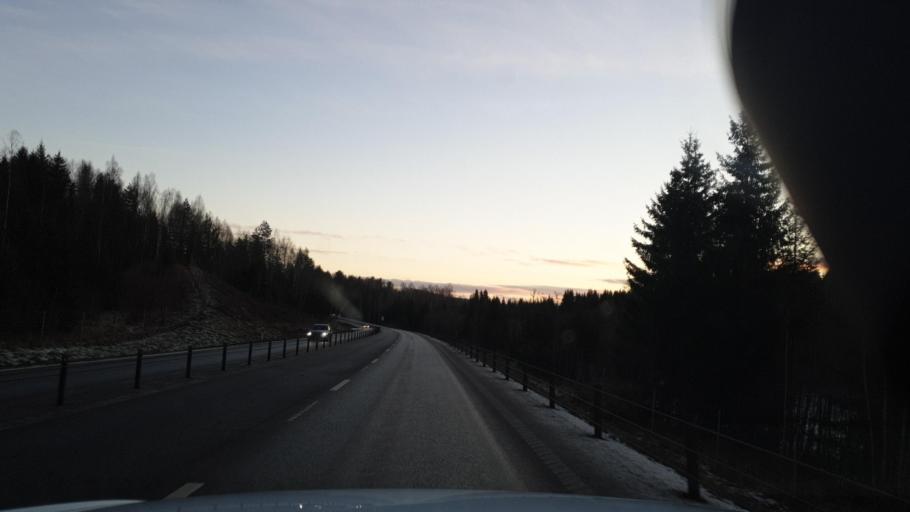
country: SE
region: Vaermland
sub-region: Arvika Kommun
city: Arvika
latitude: 59.6433
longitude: 12.7334
